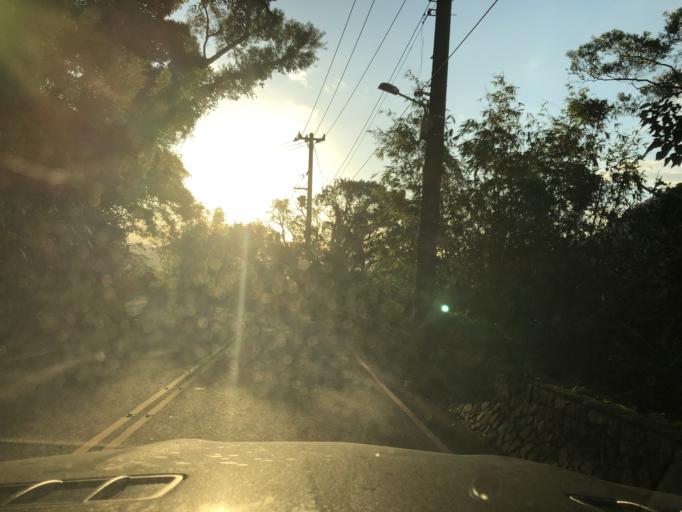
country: TW
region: Taipei
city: Taipei
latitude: 25.1423
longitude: 121.5533
